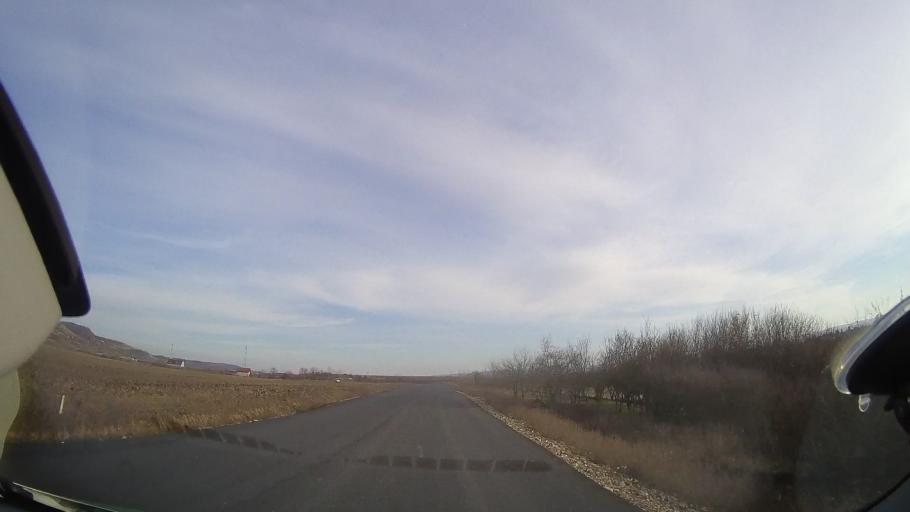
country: RO
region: Bihor
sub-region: Comuna Tileagd
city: Tileagd
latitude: 47.0830
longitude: 22.1903
